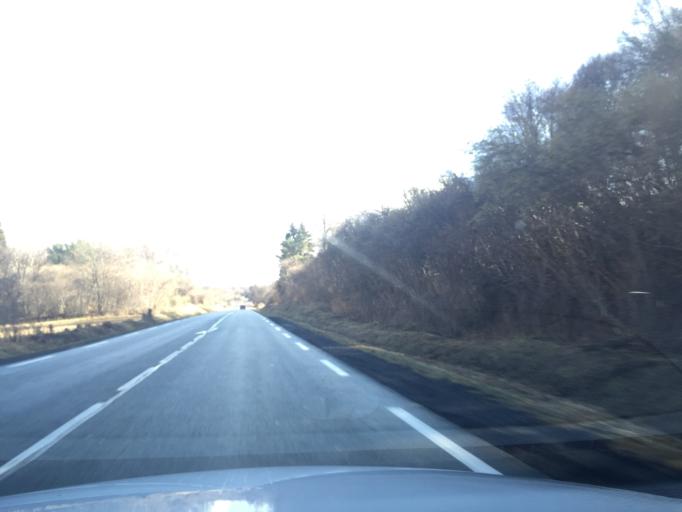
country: FR
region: Auvergne
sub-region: Departement du Puy-de-Dome
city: Orcines
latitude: 45.8053
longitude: 2.9801
